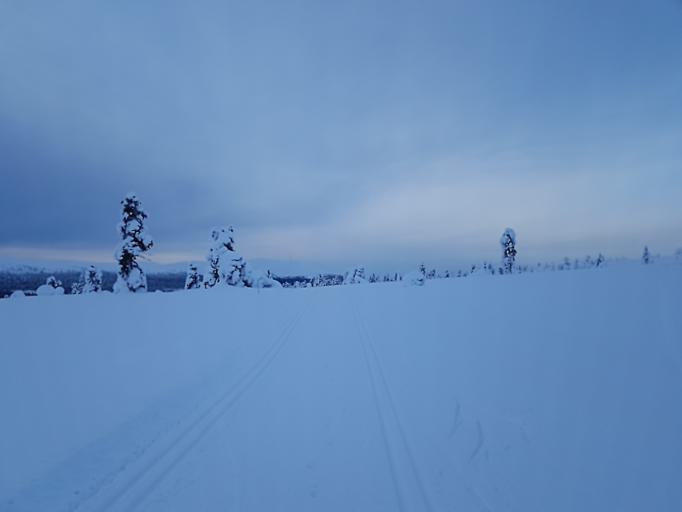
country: FI
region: Lapland
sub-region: Tunturi-Lappi
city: Kolari
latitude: 67.6570
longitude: 24.2288
